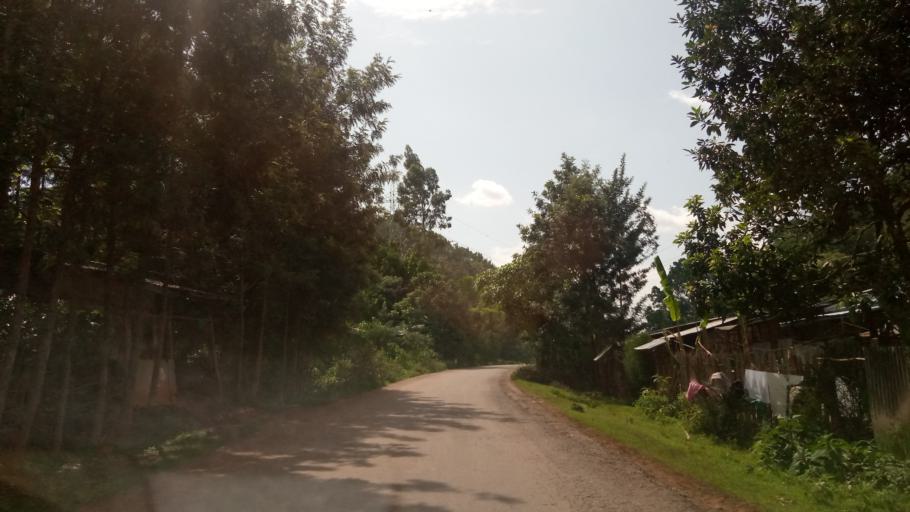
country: ET
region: Oromiya
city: Agaro
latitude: 7.9227
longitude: 36.5166
